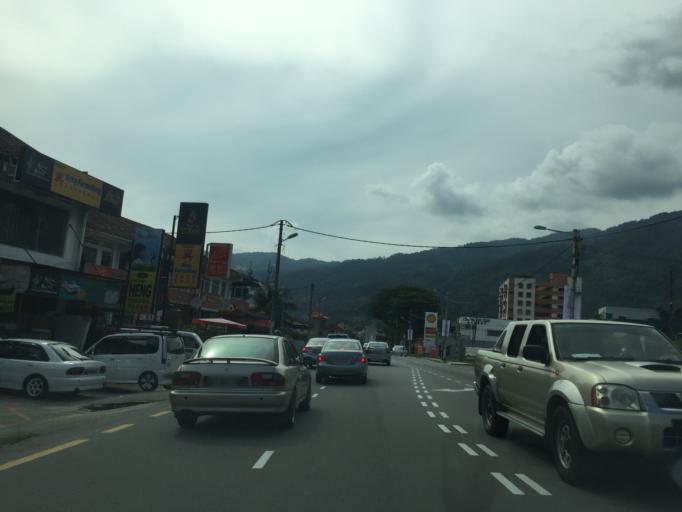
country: MY
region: Penang
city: George Town
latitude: 5.4045
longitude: 100.2884
